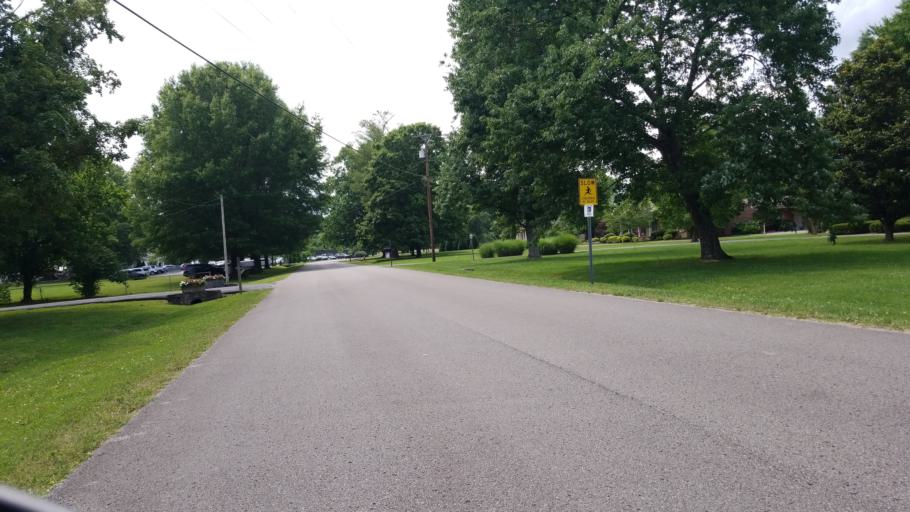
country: US
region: Tennessee
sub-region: Davidson County
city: Forest Hills
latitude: 36.0405
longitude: -86.8540
